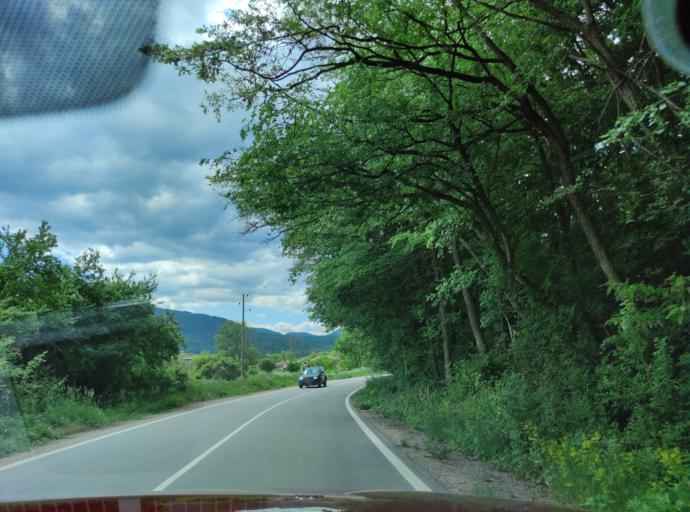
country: BG
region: Montana
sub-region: Obshtina Chiprovtsi
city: Chiprovtsi
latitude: 43.4374
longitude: 22.9456
